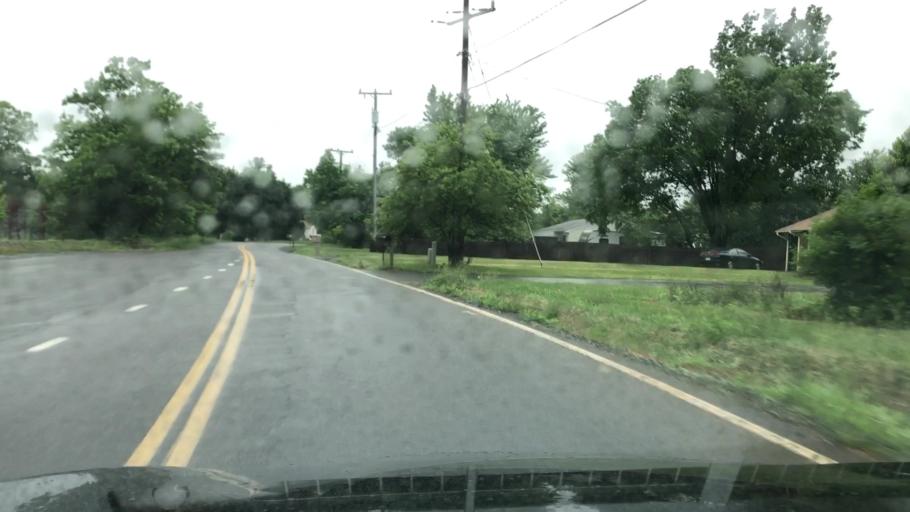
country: US
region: Virginia
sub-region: Stafford County
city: Falmouth
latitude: 38.3562
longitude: -77.5253
